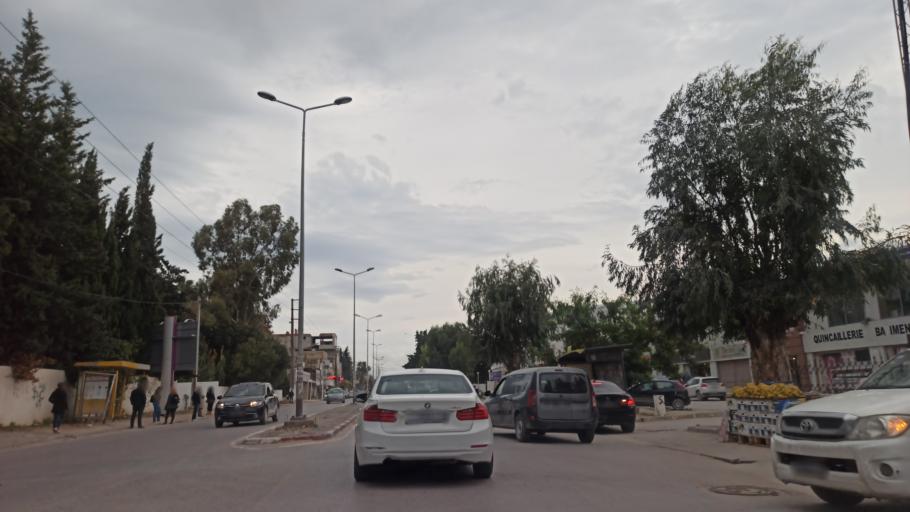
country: TN
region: Ariana
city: Ariana
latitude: 36.8711
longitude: 10.2482
